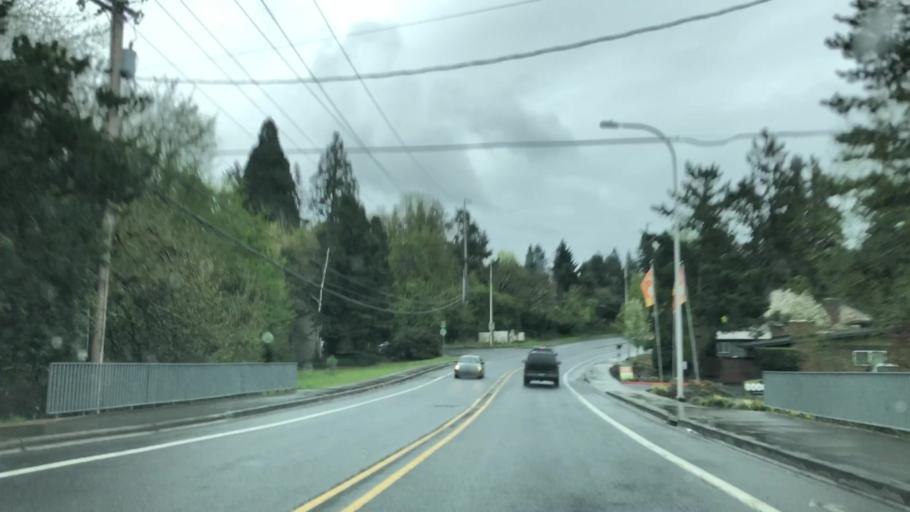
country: US
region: Oregon
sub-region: Washington County
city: Raleigh Hills
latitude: 45.4788
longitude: -122.7476
